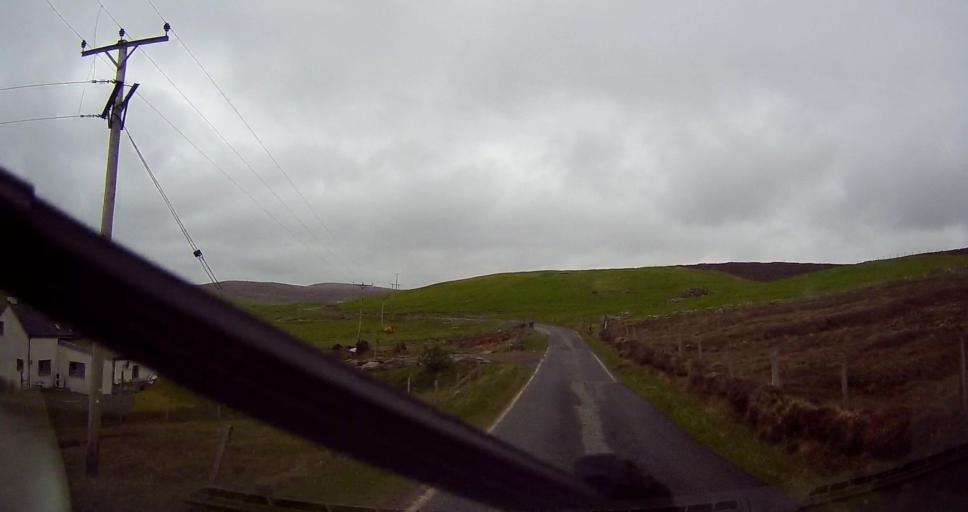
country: GB
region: Scotland
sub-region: Shetland Islands
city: Lerwick
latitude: 60.2994
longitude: -1.3580
